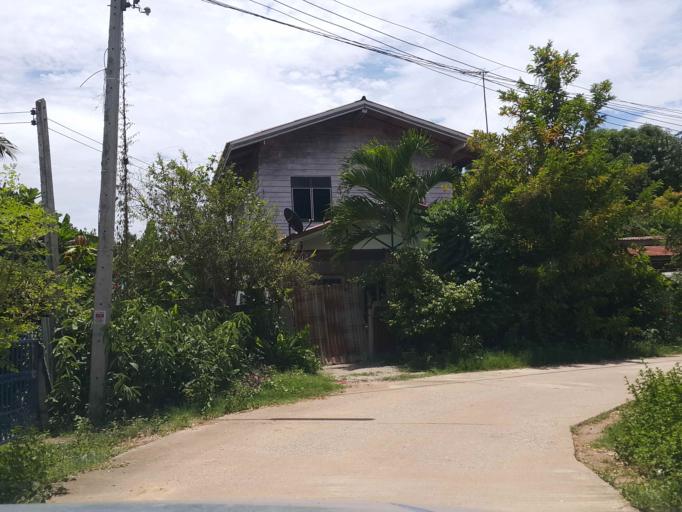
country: TH
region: Sukhothai
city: Ban Na
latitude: 17.0218
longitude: 99.7069
